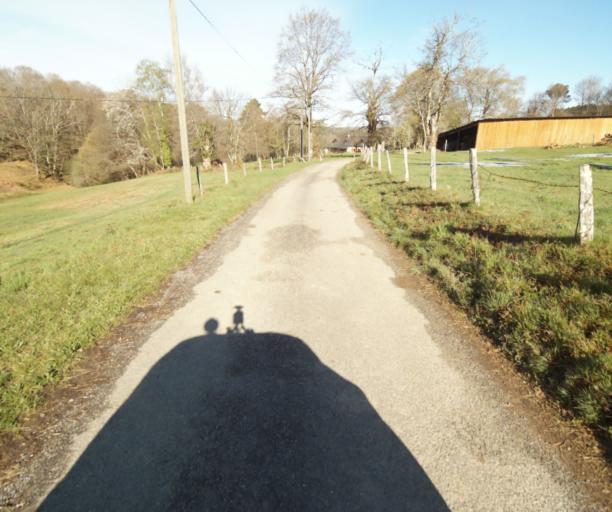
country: FR
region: Limousin
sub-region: Departement de la Correze
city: Laguenne
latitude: 45.2699
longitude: 1.8559
